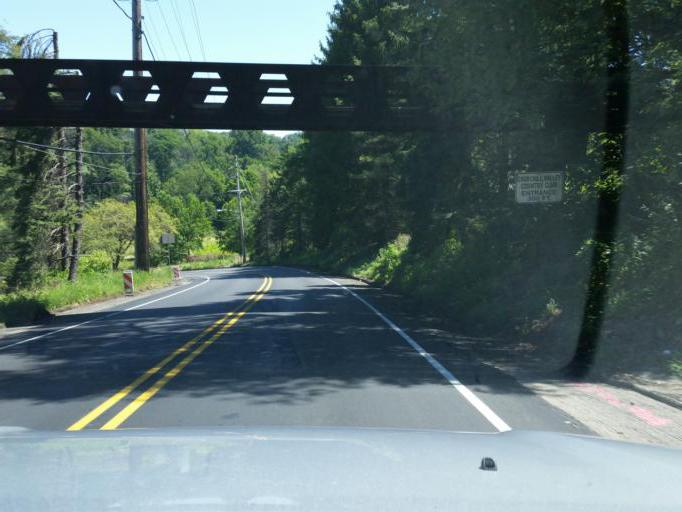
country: US
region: Pennsylvania
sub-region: Allegheny County
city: Churchill
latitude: 40.4491
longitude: -79.8455
